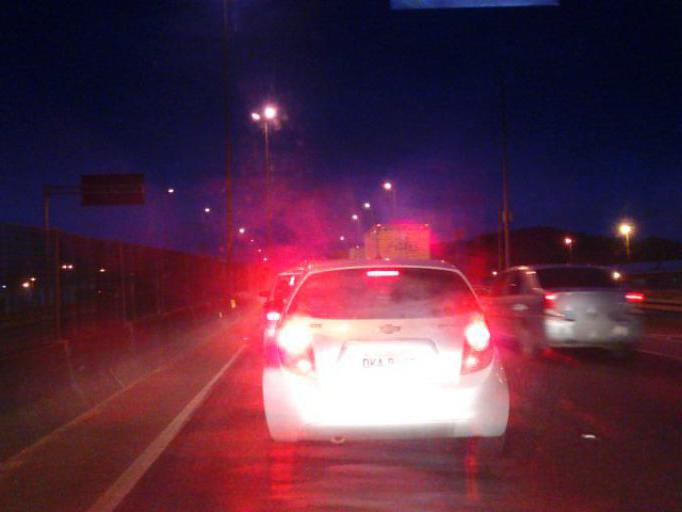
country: BR
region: Santa Catarina
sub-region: Itajai
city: Itajai
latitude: -26.8889
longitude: -48.7219
